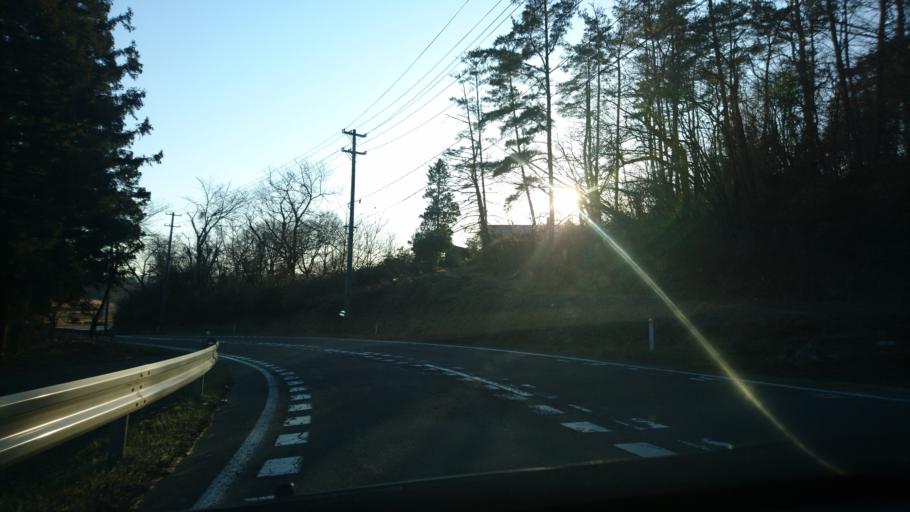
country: JP
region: Iwate
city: Ichinoseki
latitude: 39.0087
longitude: 141.3600
